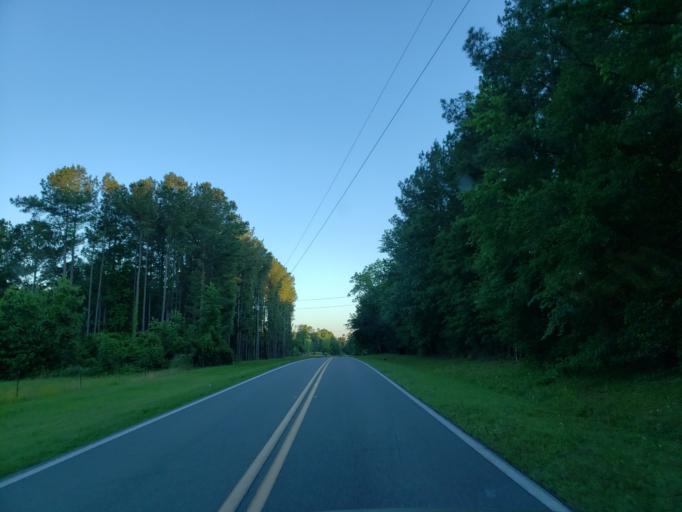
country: US
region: Florida
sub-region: Madison County
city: Madison
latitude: 30.6134
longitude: -83.2554
